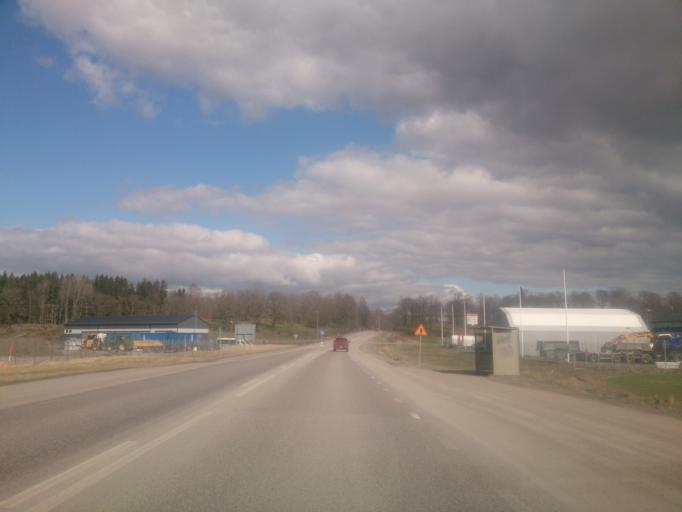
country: SE
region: OEstergoetland
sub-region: Norrkopings Kommun
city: Norrkoping
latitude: 58.5661
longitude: 16.0823
